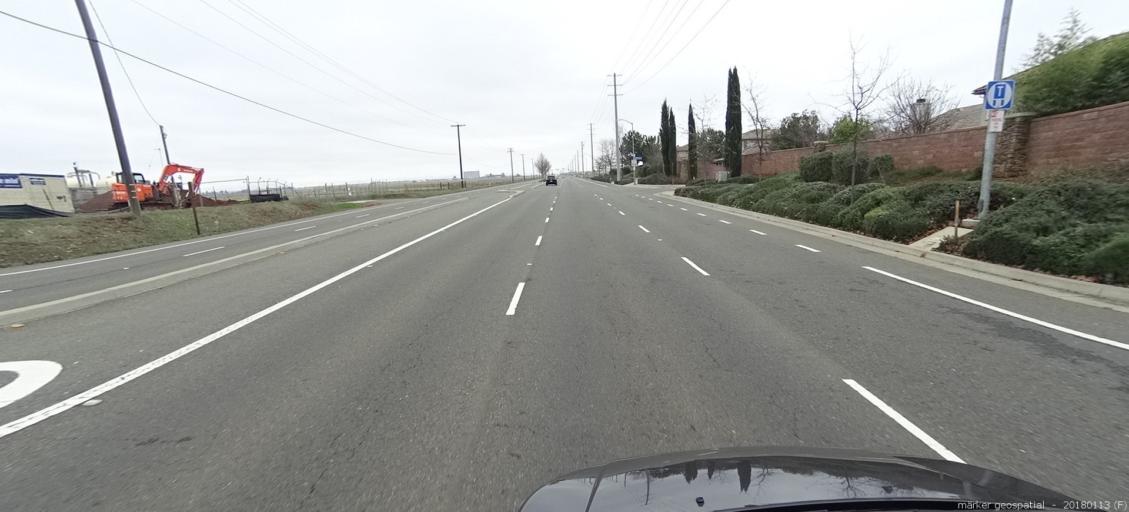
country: US
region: California
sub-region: Sacramento County
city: Gold River
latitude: 38.5593
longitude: -121.2361
